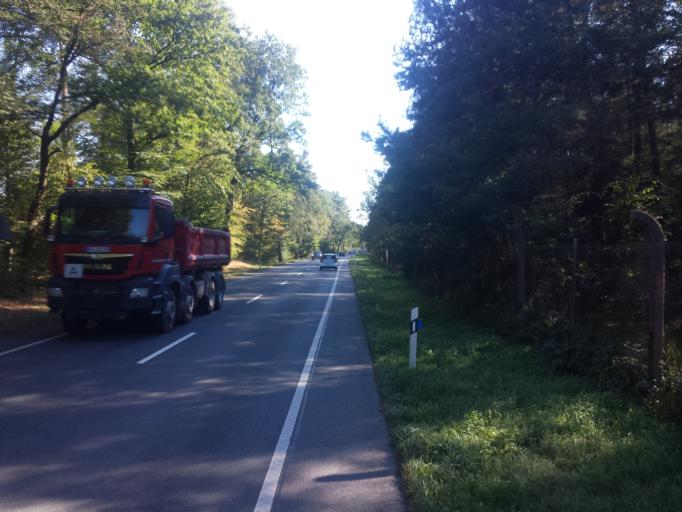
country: DE
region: Hesse
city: Viernheim
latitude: 49.5812
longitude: 8.5898
